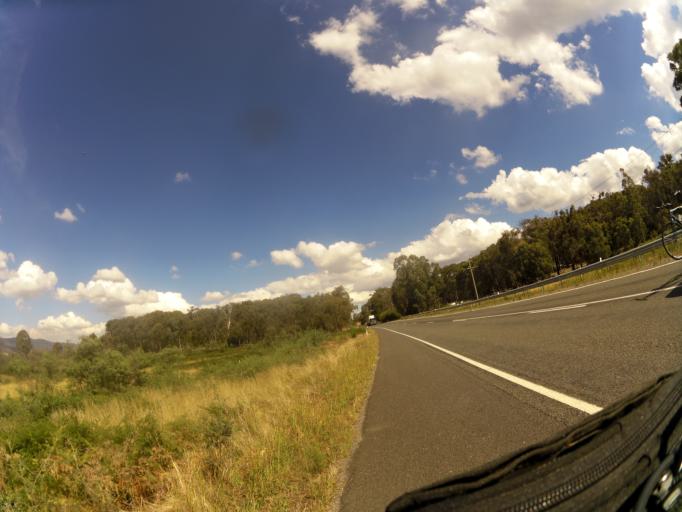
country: AU
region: Victoria
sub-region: Mansfield
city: Mansfield
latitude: -36.8772
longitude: 145.9936
